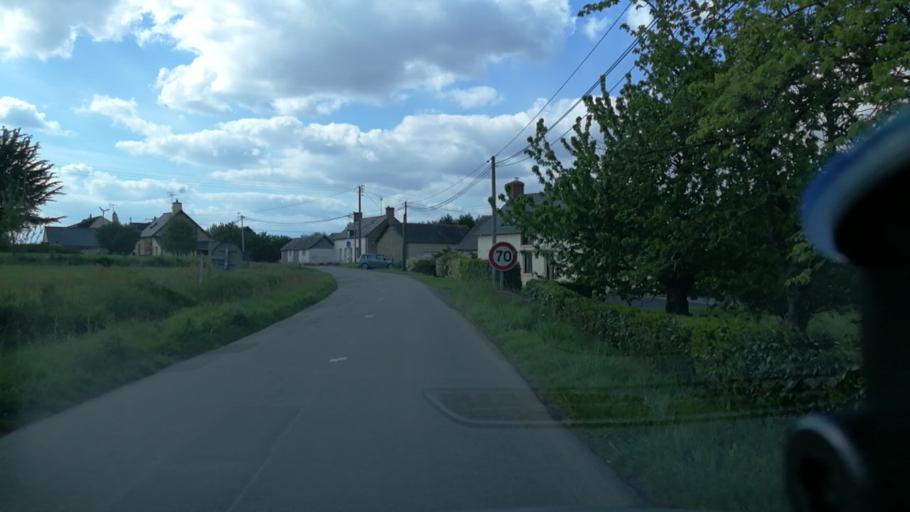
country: FR
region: Brittany
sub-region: Departement d'Ille-et-Vilaine
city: Retiers
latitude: 47.8906
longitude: -1.3354
